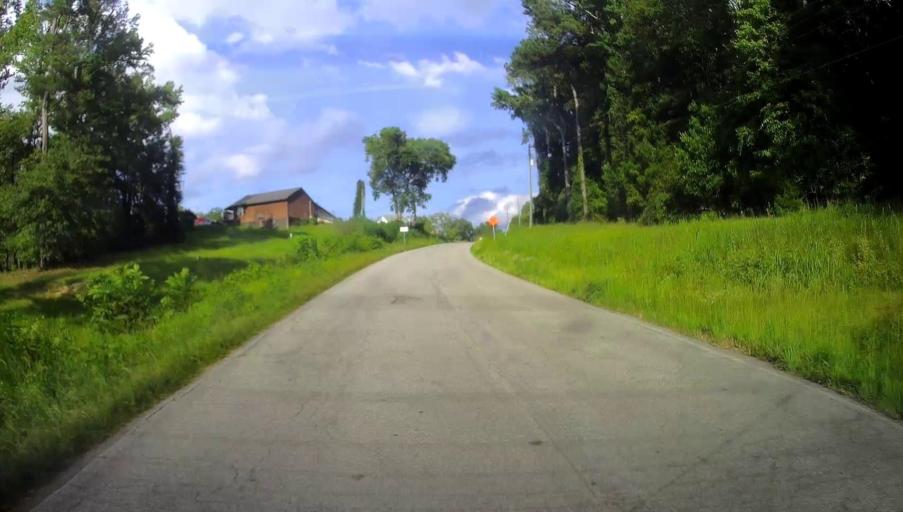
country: US
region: Georgia
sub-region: Crawford County
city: Knoxville
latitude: 32.7240
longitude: -84.0002
